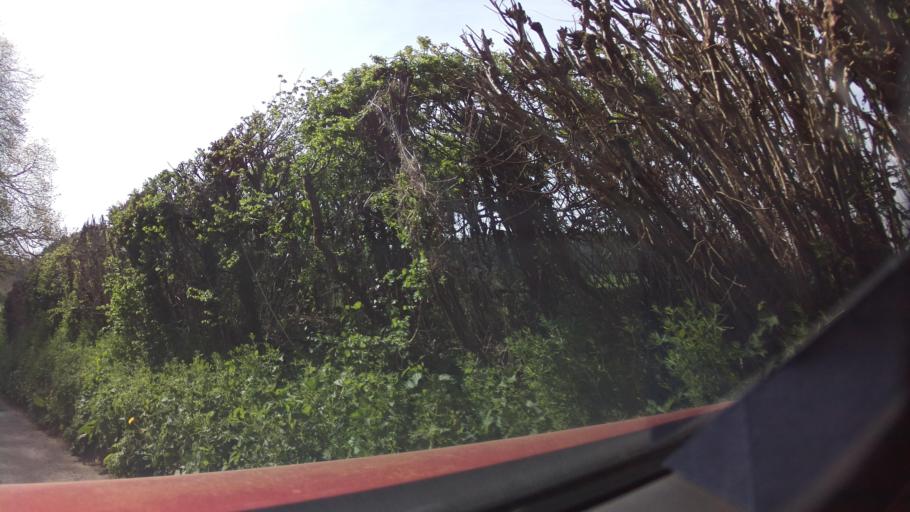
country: GB
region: England
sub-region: Dorset
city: Sherborne
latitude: 50.9778
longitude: -2.5333
